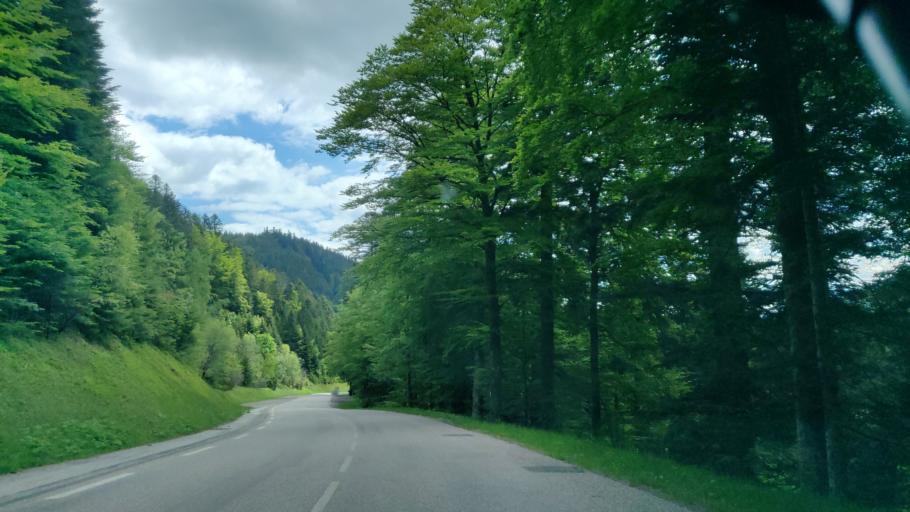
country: FR
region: Lorraine
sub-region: Departement des Vosges
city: Xonrupt-Longemer
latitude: 48.0304
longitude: 6.9621
